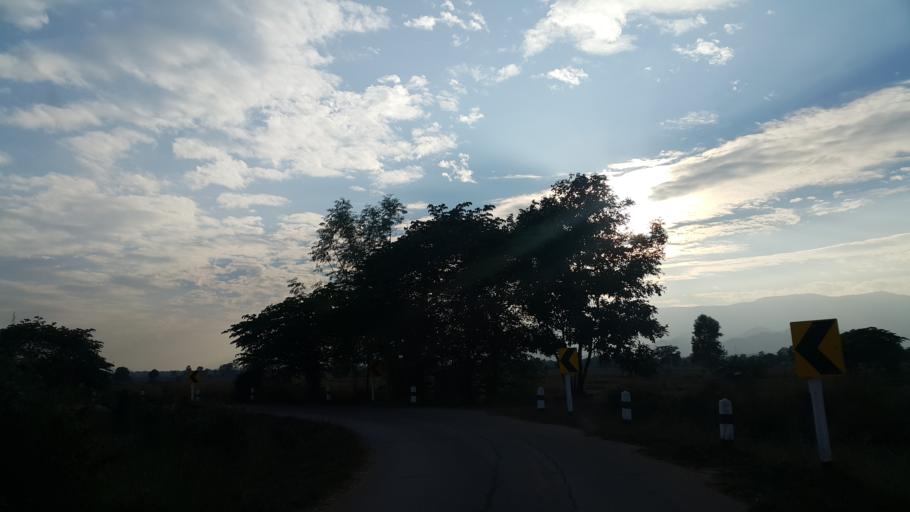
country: TH
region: Lampang
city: Sop Prap
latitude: 17.9182
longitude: 99.3277
